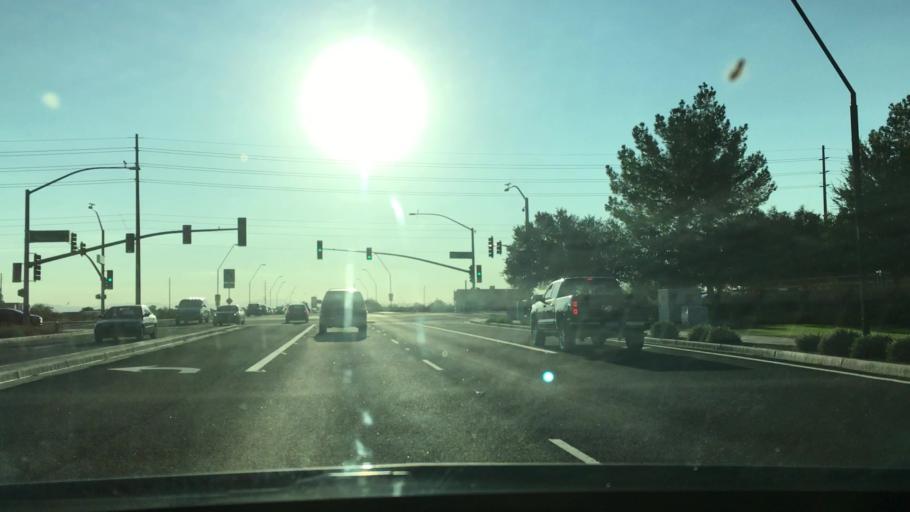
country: US
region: Arizona
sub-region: Maricopa County
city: Queen Creek
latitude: 33.2746
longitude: -111.6702
